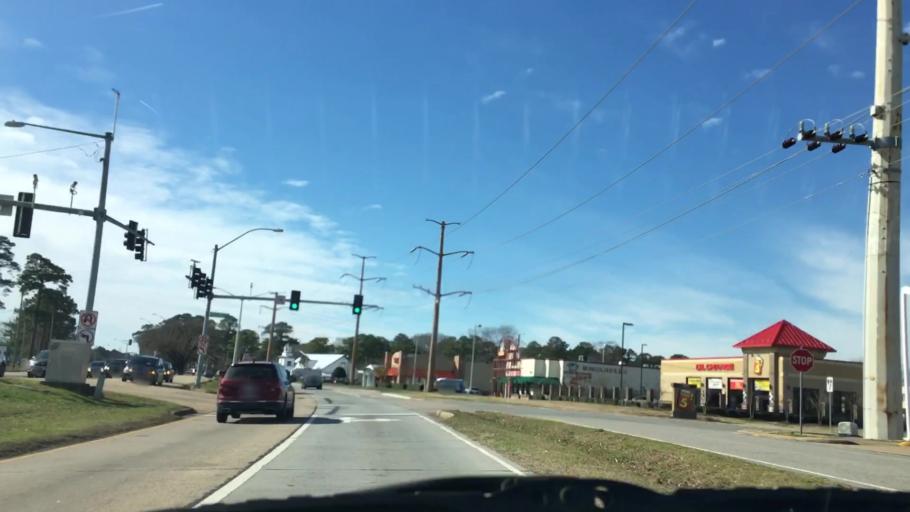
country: US
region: Virginia
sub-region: City of Virginia Beach
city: Virginia Beach
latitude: 36.8487
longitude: -76.0328
